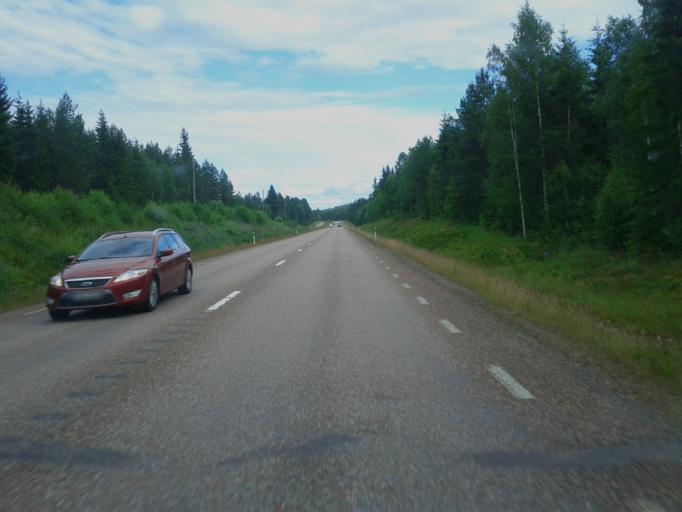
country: SE
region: Dalarna
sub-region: Faluns Kommun
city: Bjursas
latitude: 60.7433
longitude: 15.3929
